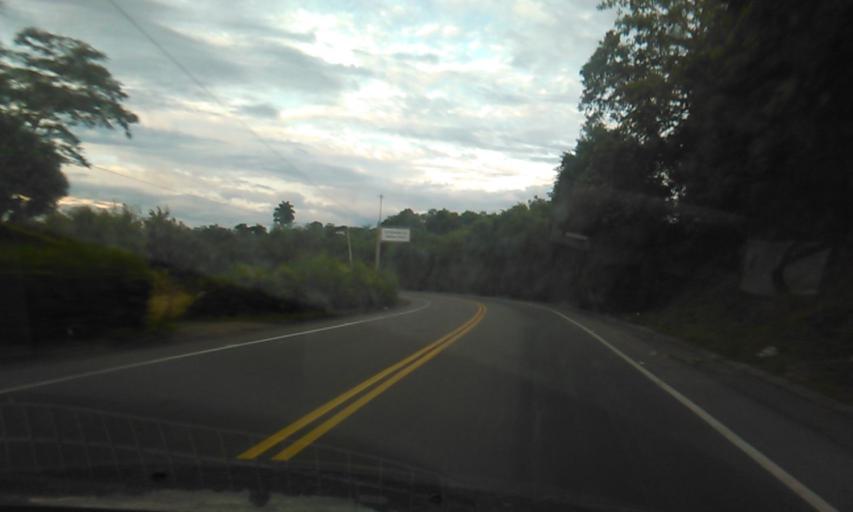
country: CO
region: Quindio
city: La Tebaida
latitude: 4.4228
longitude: -75.8624
